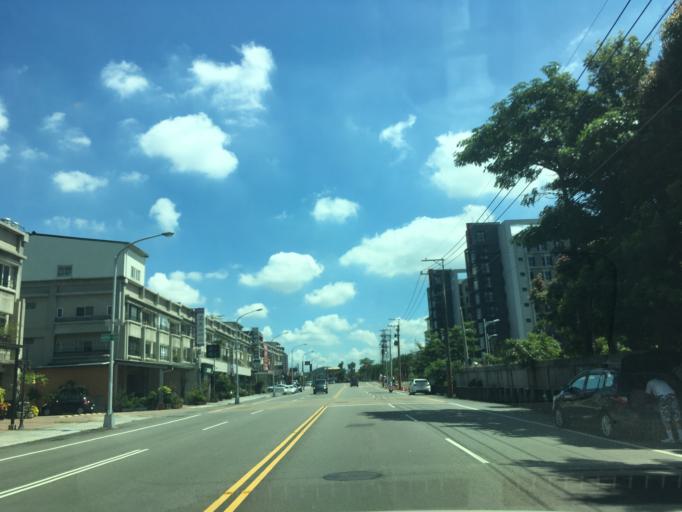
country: TW
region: Taiwan
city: Fengyuan
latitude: 24.2007
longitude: 120.7223
